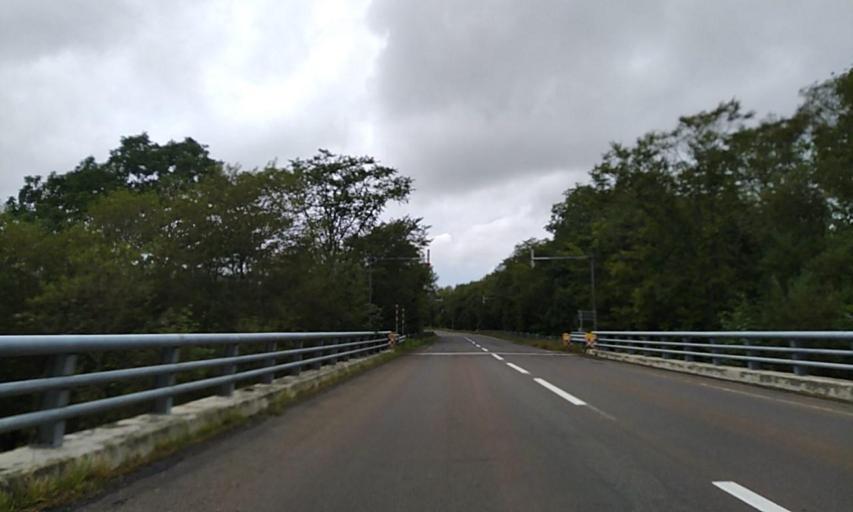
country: JP
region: Hokkaido
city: Bihoro
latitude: 43.5180
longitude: 144.4233
